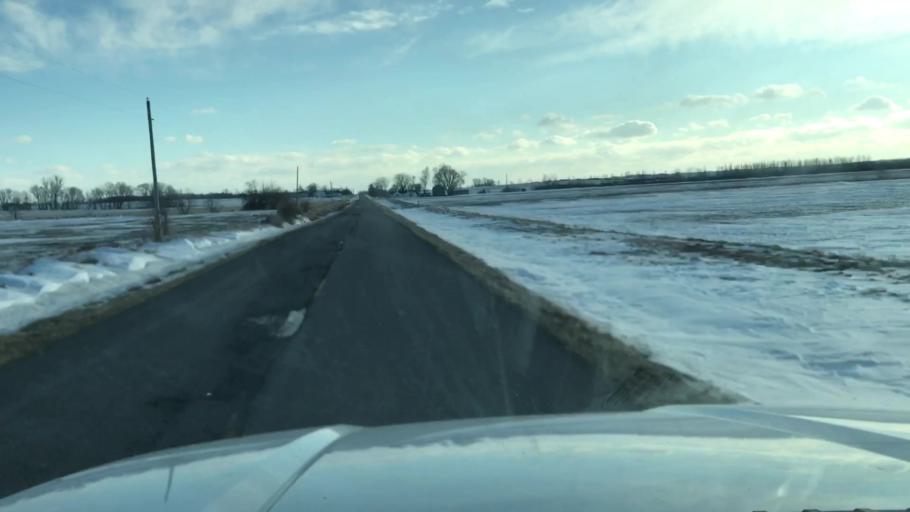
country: US
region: Missouri
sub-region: Holt County
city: Oregon
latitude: 40.1229
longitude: -95.0226
